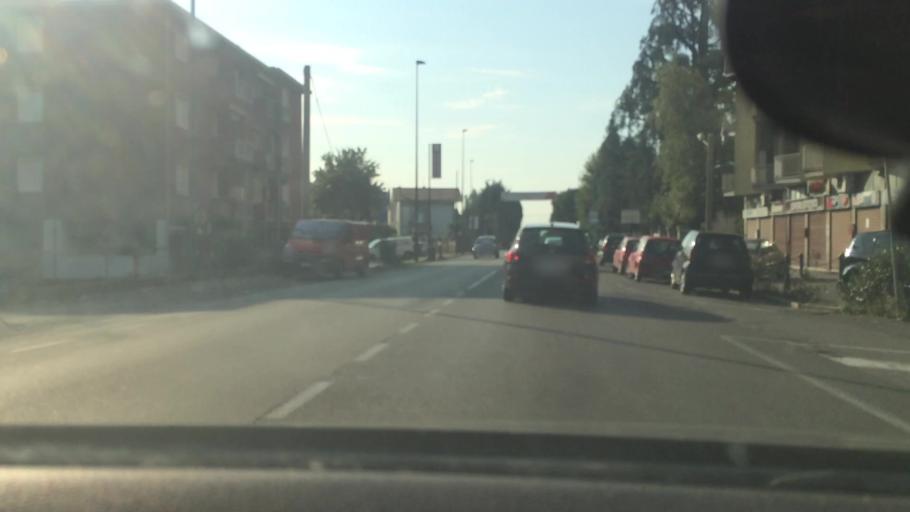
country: IT
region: Lombardy
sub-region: Provincia di Varese
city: Gerenzano
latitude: 45.6394
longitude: 9.0059
